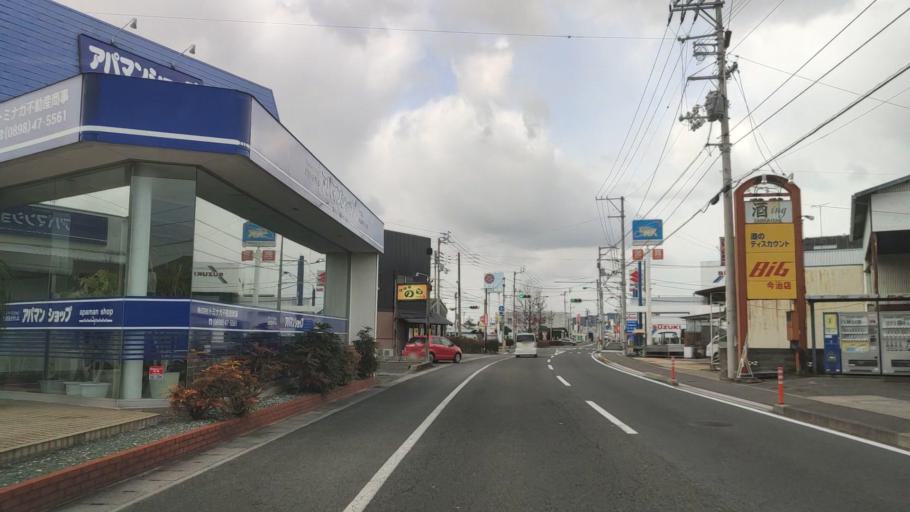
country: JP
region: Ehime
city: Saijo
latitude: 34.0442
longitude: 133.0225
